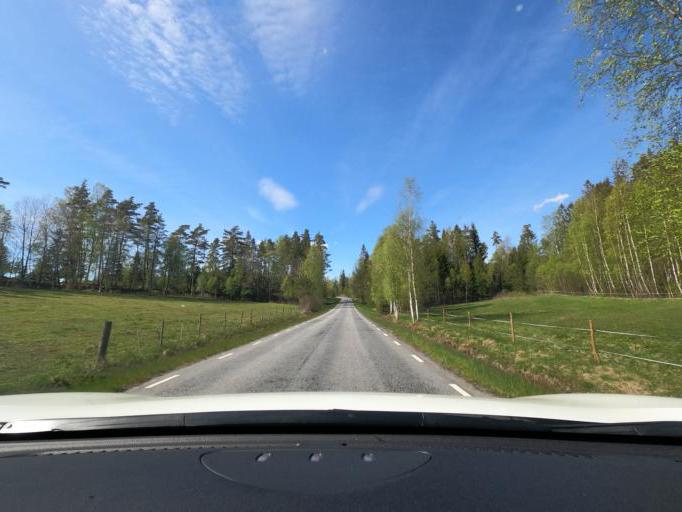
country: SE
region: Vaestra Goetaland
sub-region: Marks Kommun
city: Bua
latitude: 57.4855
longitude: 12.5655
